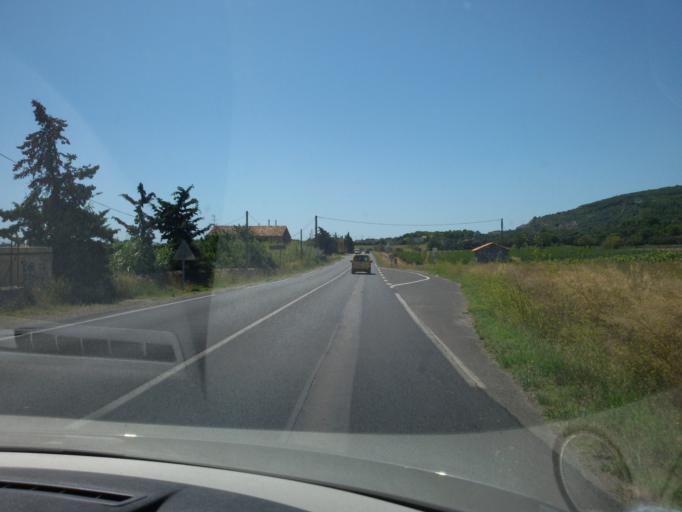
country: FR
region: Languedoc-Roussillon
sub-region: Departement de l'Herault
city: Frontignan
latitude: 43.4729
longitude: 3.7695
